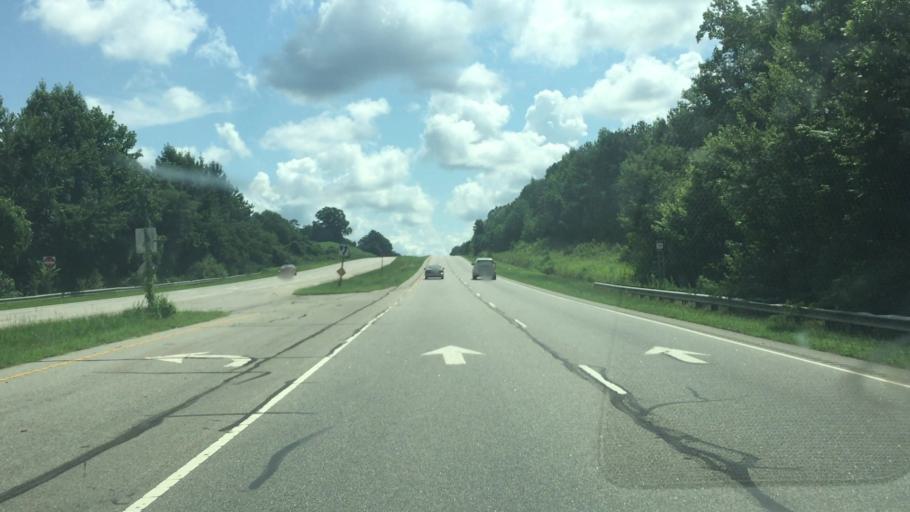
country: US
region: North Carolina
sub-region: Anson County
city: Wadesboro
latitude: 34.9629
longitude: -80.0038
